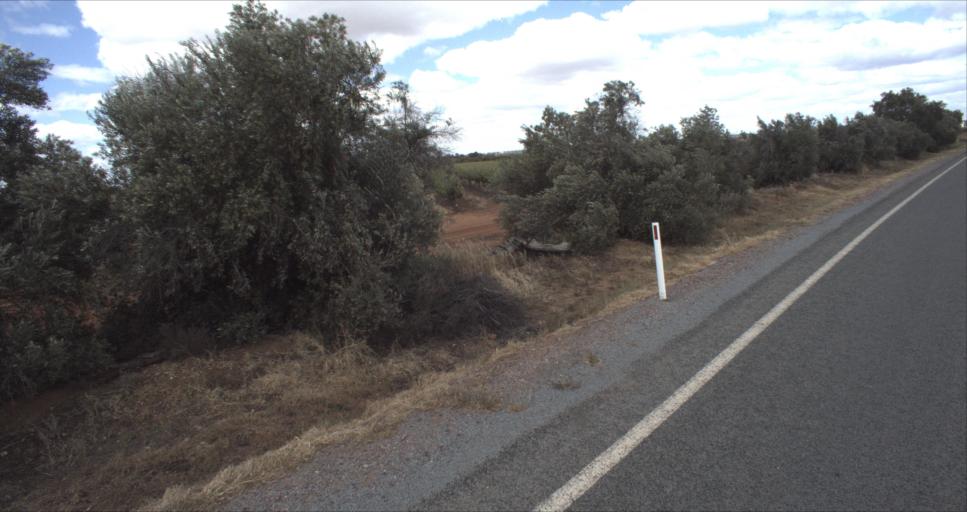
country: AU
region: New South Wales
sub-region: Leeton
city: Leeton
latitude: -34.5811
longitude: 146.4005
